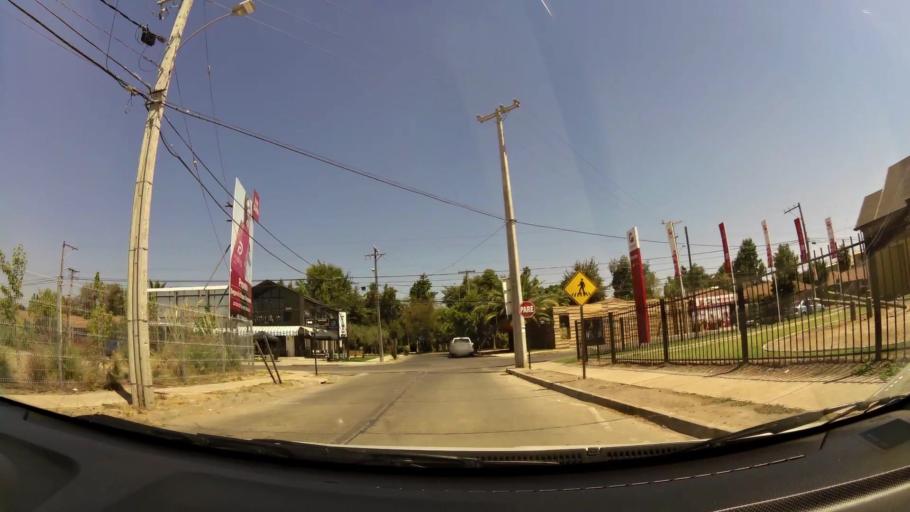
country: CL
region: Maule
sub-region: Provincia de Talca
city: Talca
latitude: -35.4297
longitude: -71.6187
